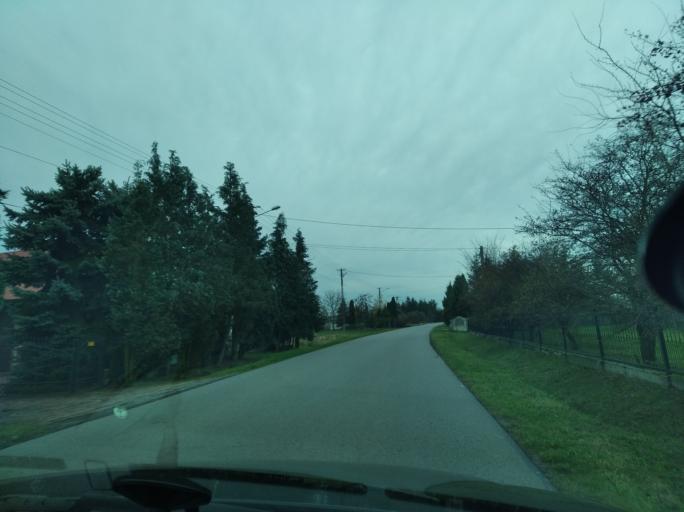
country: PL
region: Subcarpathian Voivodeship
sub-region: Powiat przeworski
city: Nowosielce
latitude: 50.0936
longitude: 22.4120
